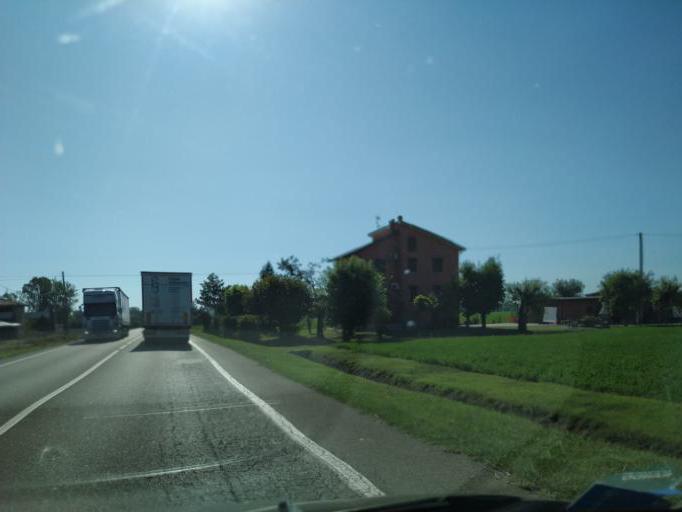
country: IT
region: Emilia-Romagna
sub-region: Provincia di Bologna
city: San Giovanni in Persiceto
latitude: 44.6492
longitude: 11.1589
